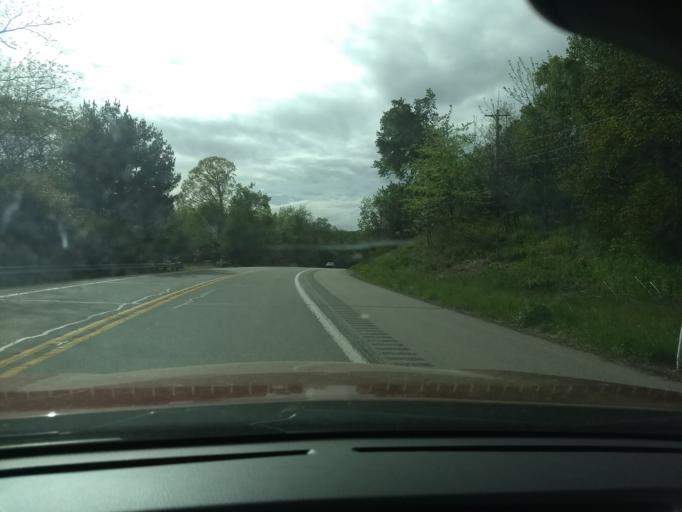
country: US
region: Pennsylvania
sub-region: Allegheny County
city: Russellton
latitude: 40.5824
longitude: -79.8789
